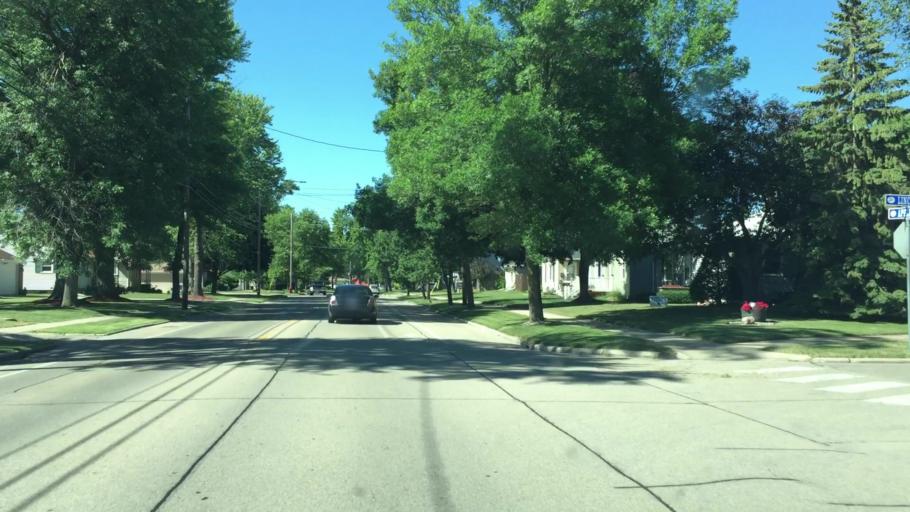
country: US
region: Wisconsin
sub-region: Winnebago County
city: Menasha
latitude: 44.2138
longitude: -88.4346
